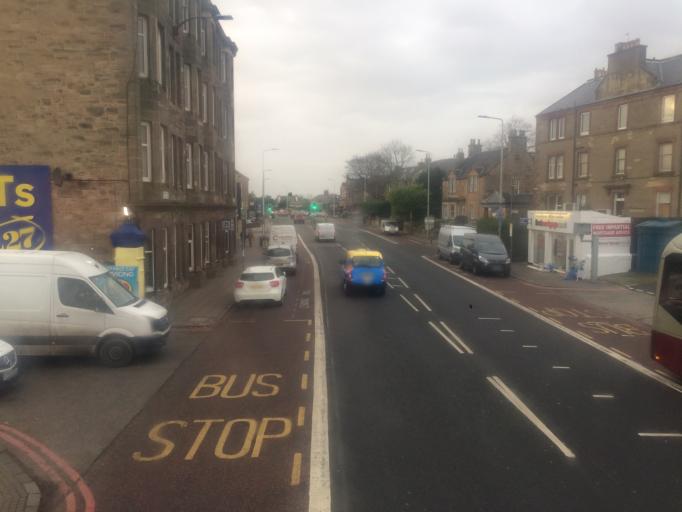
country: GB
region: Scotland
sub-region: Edinburgh
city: Colinton
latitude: 55.9431
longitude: -3.2869
